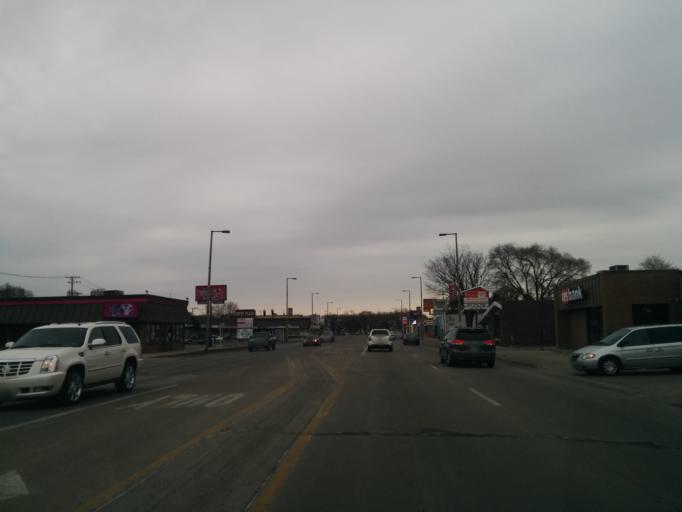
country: US
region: Illinois
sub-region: Cook County
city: Westchester
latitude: 41.8528
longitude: -87.8820
